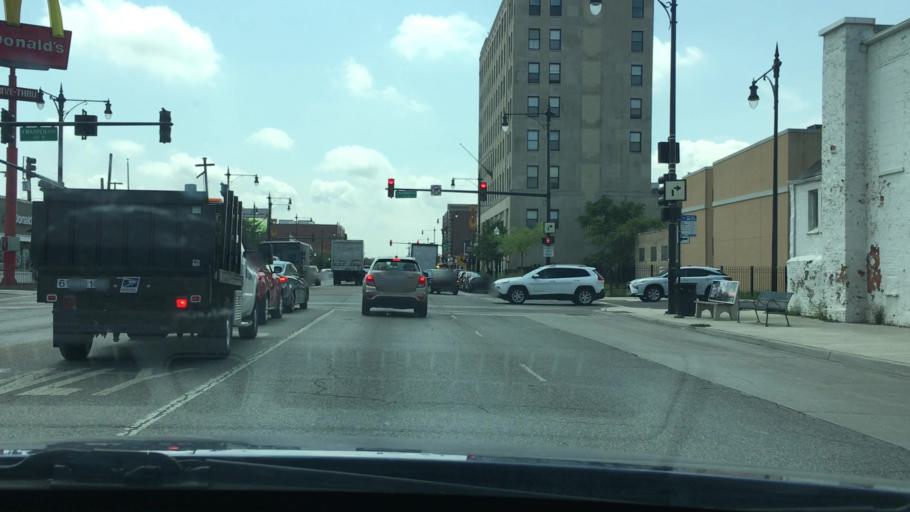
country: US
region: Illinois
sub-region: Cook County
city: Chicago
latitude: 41.8824
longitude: -87.6865
